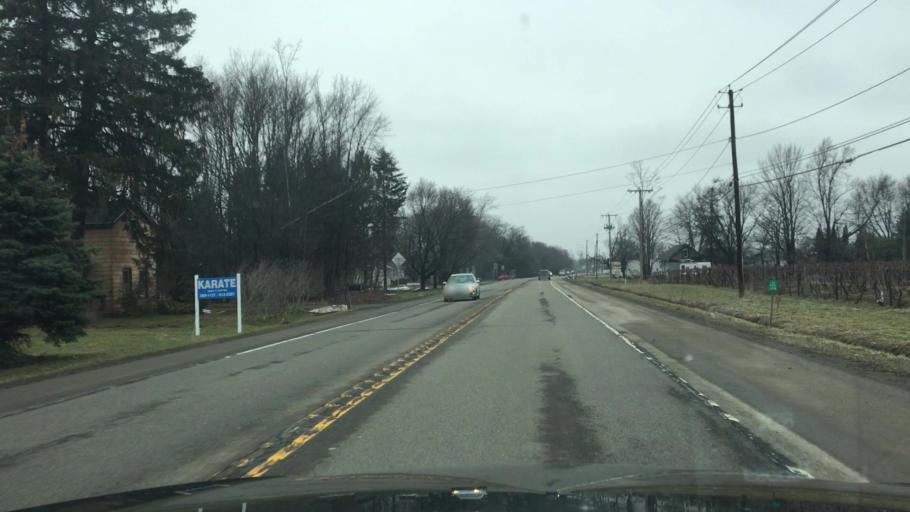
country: US
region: New York
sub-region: Chautauqua County
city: Fredonia
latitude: 42.4236
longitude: -79.3057
